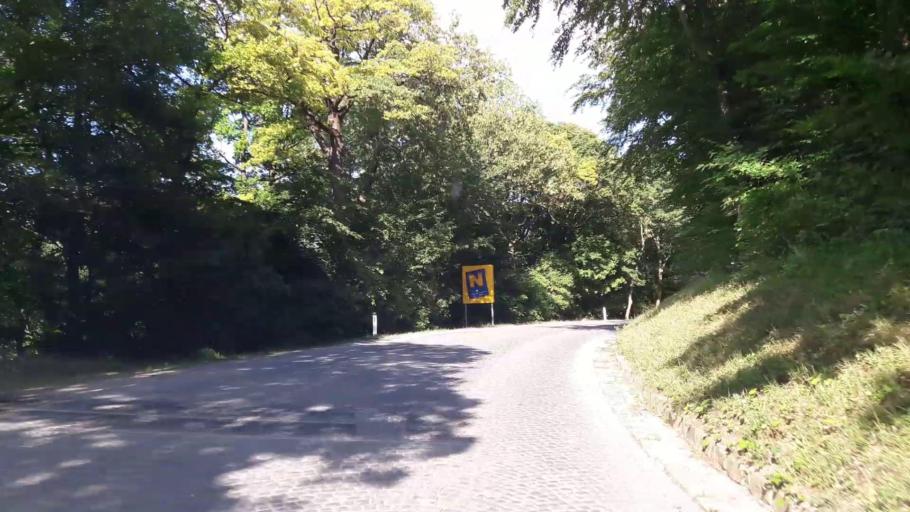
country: AT
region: Lower Austria
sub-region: Politischer Bezirk Wien-Umgebung
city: Klosterneuburg
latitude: 48.2815
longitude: 16.3322
